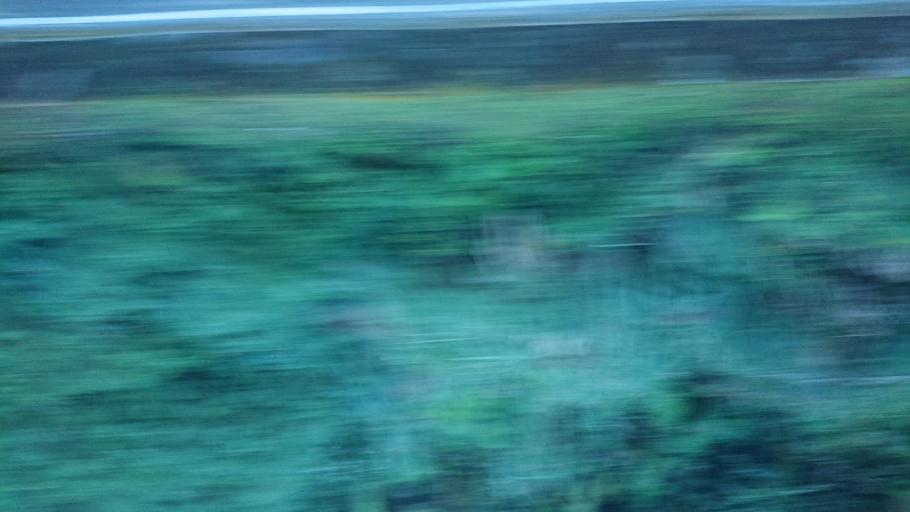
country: TW
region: Taiwan
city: Lugu
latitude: 23.4749
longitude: 120.8506
